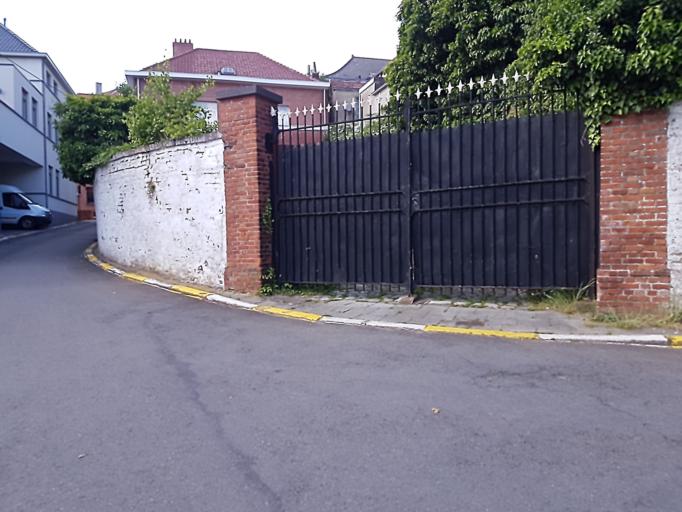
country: BE
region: Flanders
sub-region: Provincie Vlaams-Brabant
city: Overijse
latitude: 50.7724
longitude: 4.5362
